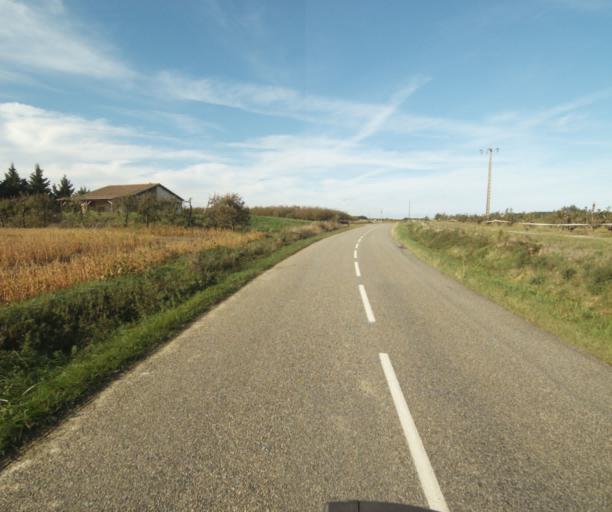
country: FR
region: Midi-Pyrenees
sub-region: Departement du Tarn-et-Garonne
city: Finhan
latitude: 43.9165
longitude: 1.1190
